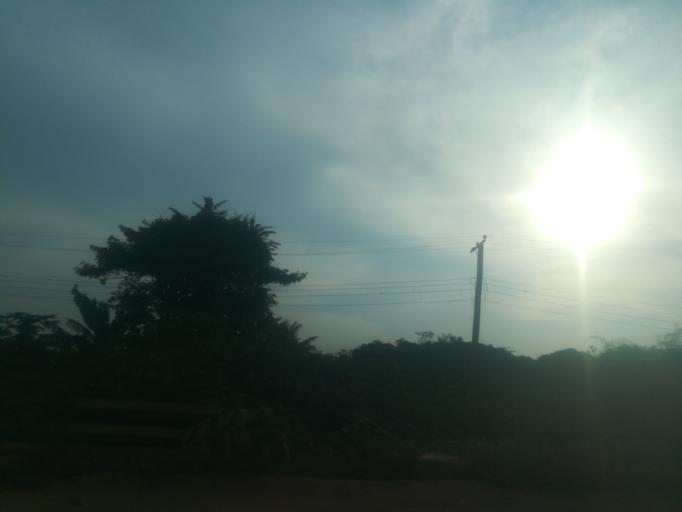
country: NG
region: Ogun
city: Abeokuta
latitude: 7.1586
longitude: 3.3233
